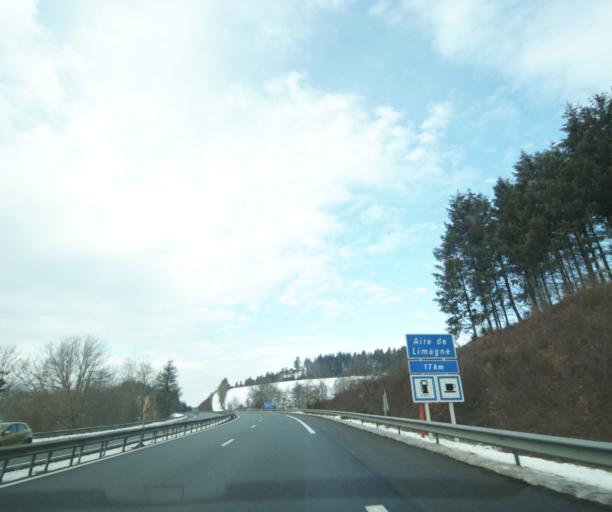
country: FR
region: Auvergne
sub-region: Departement du Puy-de-Dome
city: Saint-Remy-sur-Durolle
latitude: 45.8829
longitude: 3.6070
